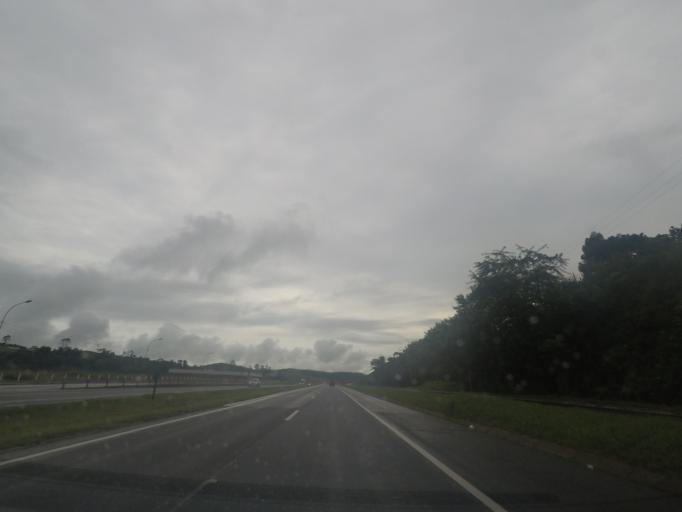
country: BR
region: Sao Paulo
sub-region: Jacupiranga
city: Jacupiranga
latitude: -24.7058
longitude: -48.0137
